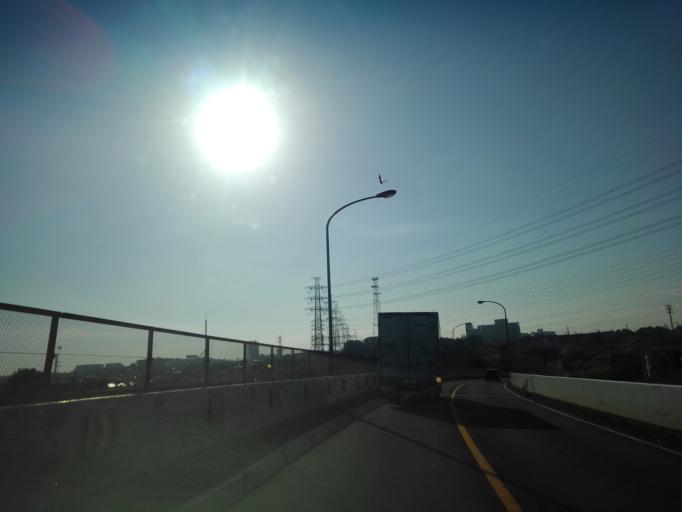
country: JP
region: Tokyo
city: Hachioji
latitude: 35.6805
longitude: 139.3538
